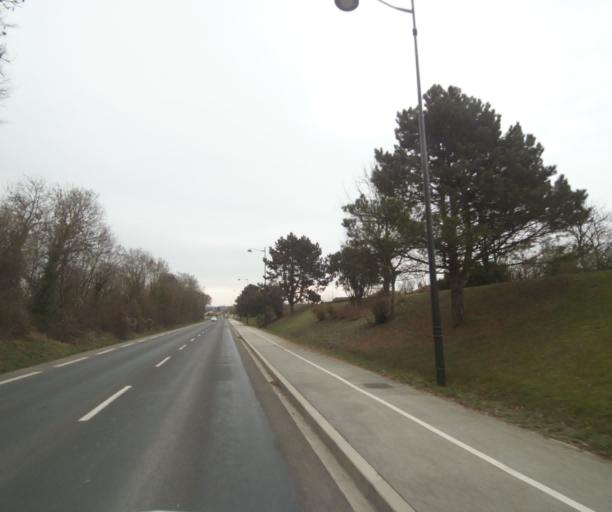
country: FR
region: Champagne-Ardenne
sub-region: Departement de la Haute-Marne
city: Bettancourt-la-Ferree
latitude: 48.6260
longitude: 4.9776
